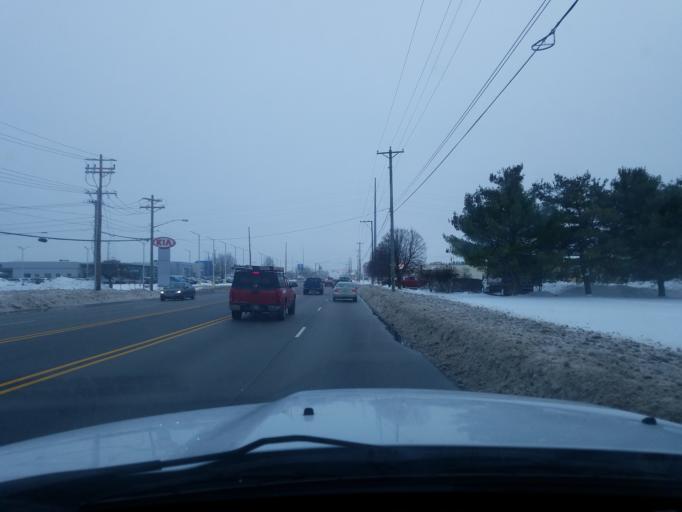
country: US
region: Indiana
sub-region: Saint Joseph County
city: Mishawaka
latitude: 41.6978
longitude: -86.1875
